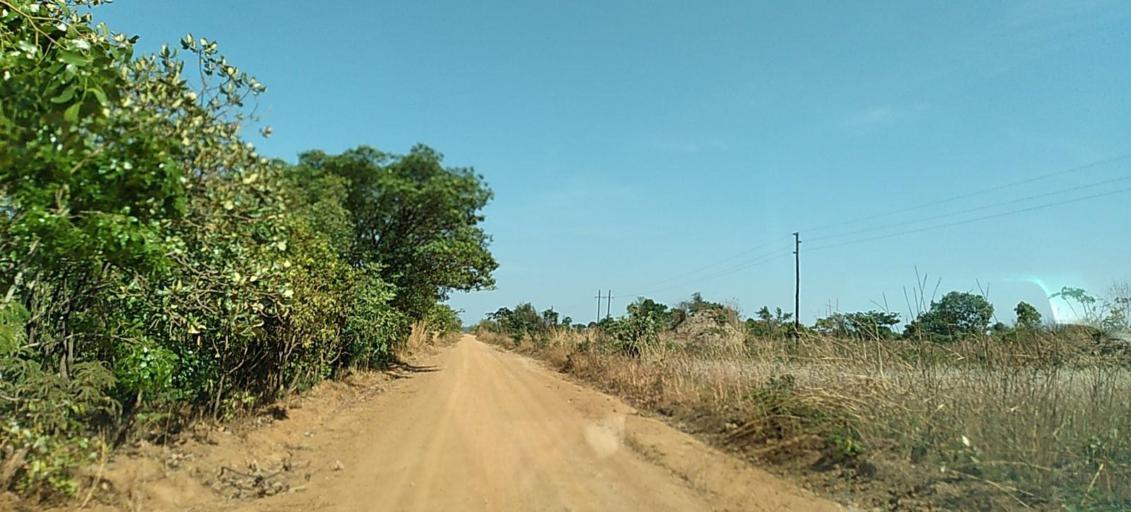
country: ZM
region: Copperbelt
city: Chililabombwe
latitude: -12.3475
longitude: 27.8781
